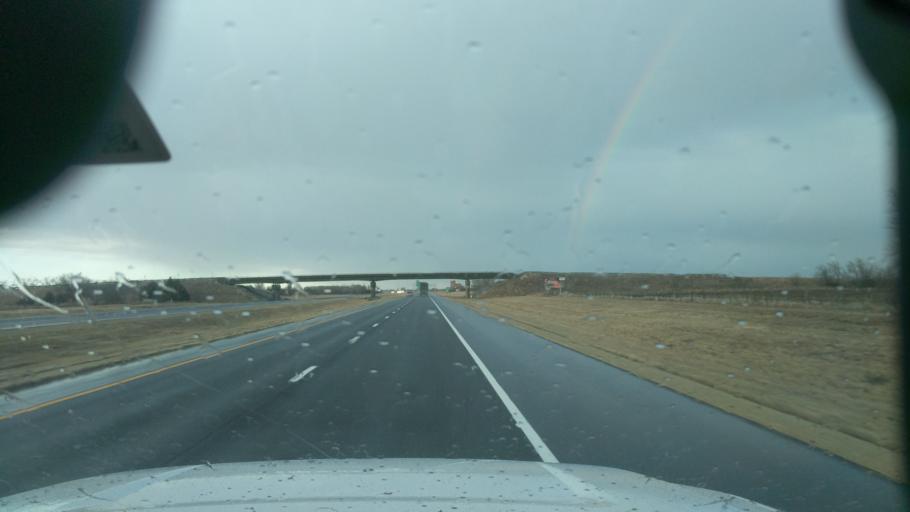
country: US
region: Kansas
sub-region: Harvey County
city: Newton
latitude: 38.0118
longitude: -97.3278
